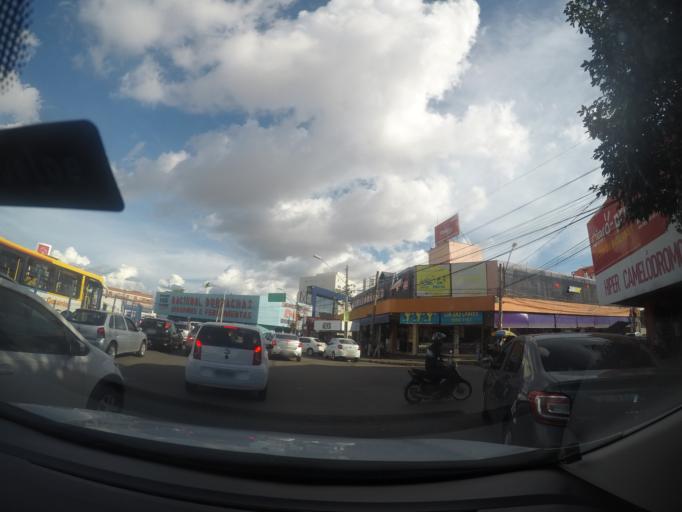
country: BR
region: Goias
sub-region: Goiania
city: Goiania
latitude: -16.6738
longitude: -49.2850
